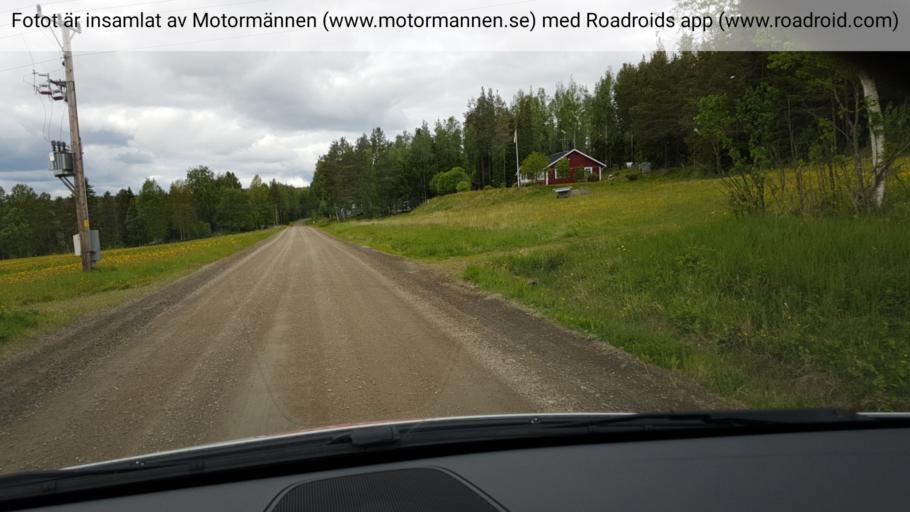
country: SE
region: Jaemtland
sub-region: Braecke Kommun
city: Braecke
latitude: 62.8665
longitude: 15.1808
